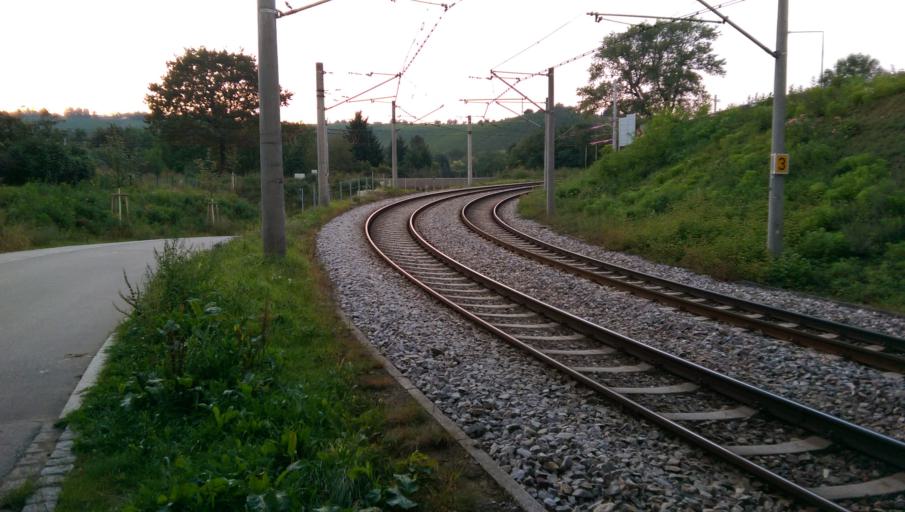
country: DE
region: Baden-Wuerttemberg
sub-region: Regierungsbezirk Stuttgart
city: Stuttgart Muehlhausen
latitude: 48.8251
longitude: 9.2112
